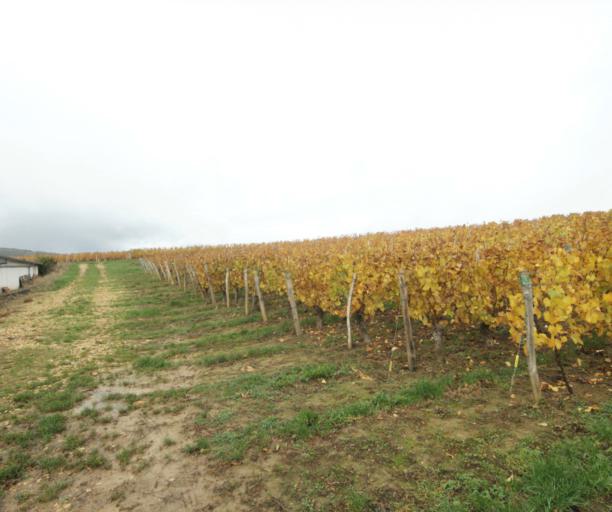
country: FR
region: Rhone-Alpes
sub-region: Departement de l'Ain
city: Pont-de-Vaux
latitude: 46.4750
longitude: 4.8713
